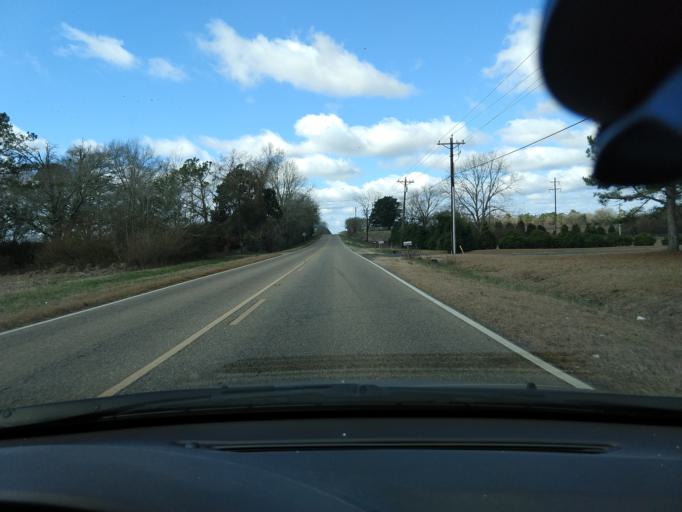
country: US
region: Alabama
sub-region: Coffee County
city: New Brockton
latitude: 31.3128
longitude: -85.9512
